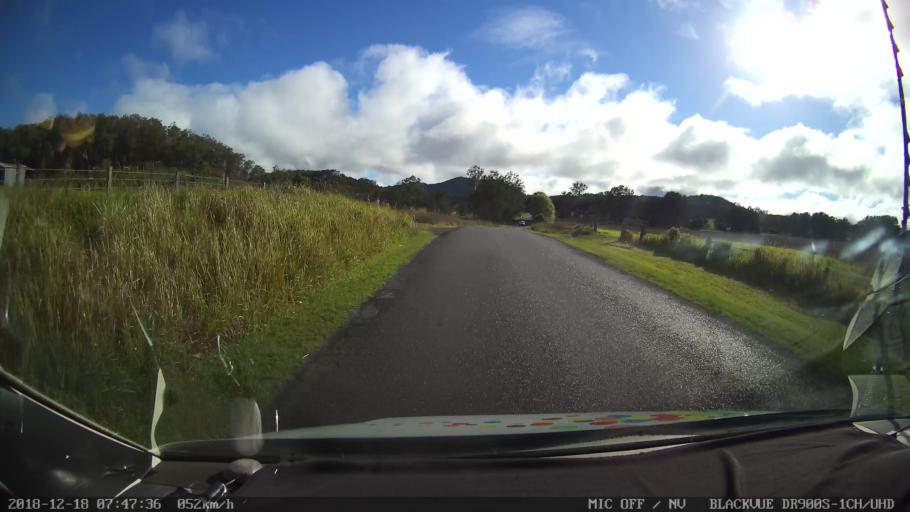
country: AU
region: New South Wales
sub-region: Kyogle
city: Kyogle
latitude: -28.4629
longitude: 152.5587
